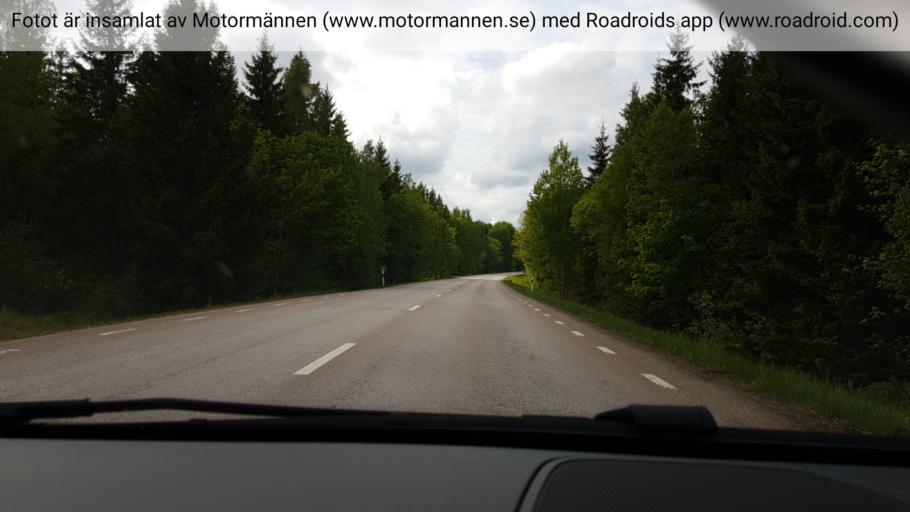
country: SE
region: Uppsala
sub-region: Osthammars Kommun
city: Osterbybruk
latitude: 60.1957
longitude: 17.8203
